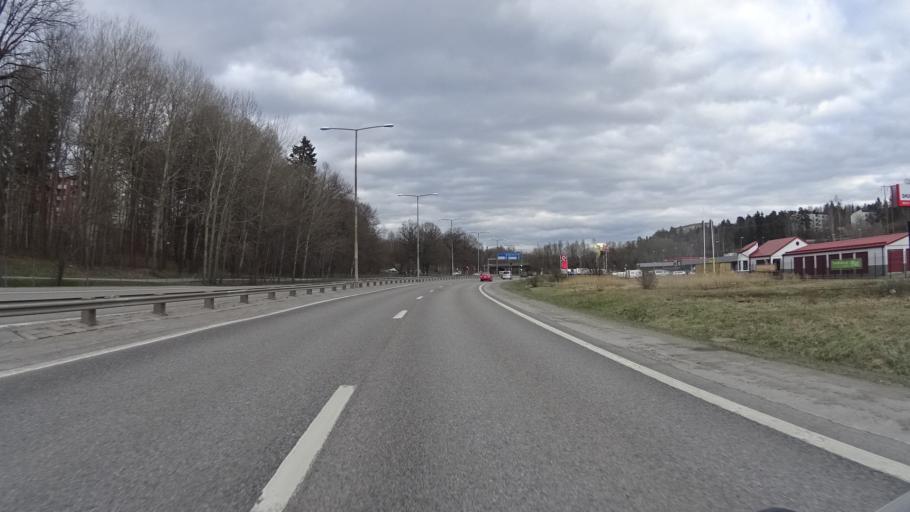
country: SE
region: Stockholm
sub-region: Stockholms Kommun
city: Arsta
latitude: 59.2621
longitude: 18.0324
